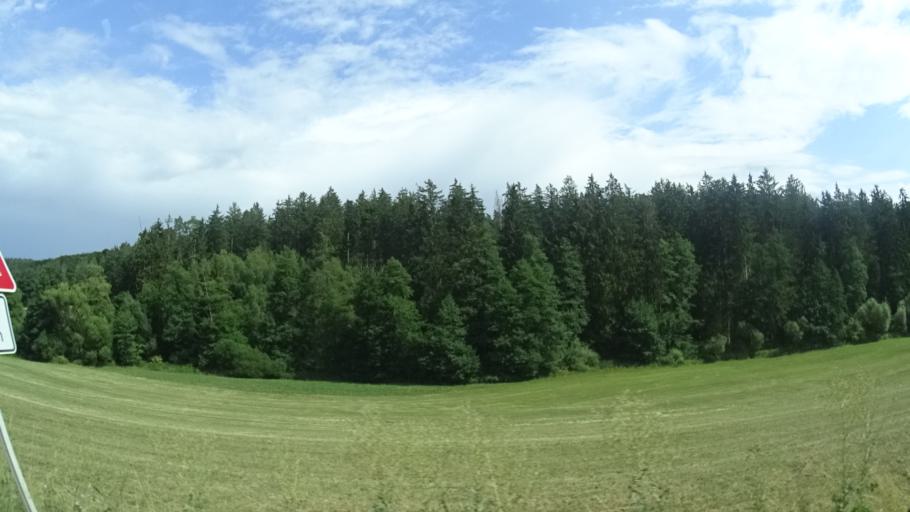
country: DE
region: Hesse
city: Grebenau
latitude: 50.7313
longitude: 9.4685
